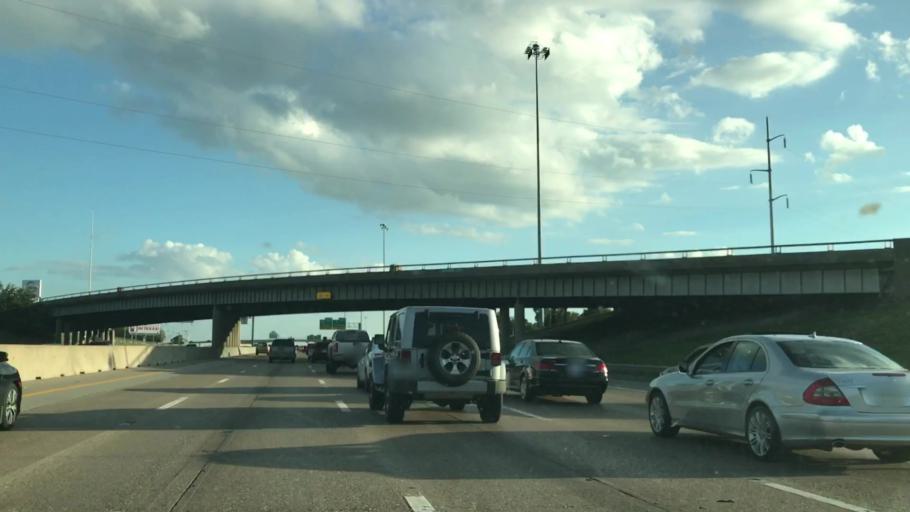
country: US
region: Texas
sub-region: Dallas County
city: Mesquite
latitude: 32.8328
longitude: -96.6319
